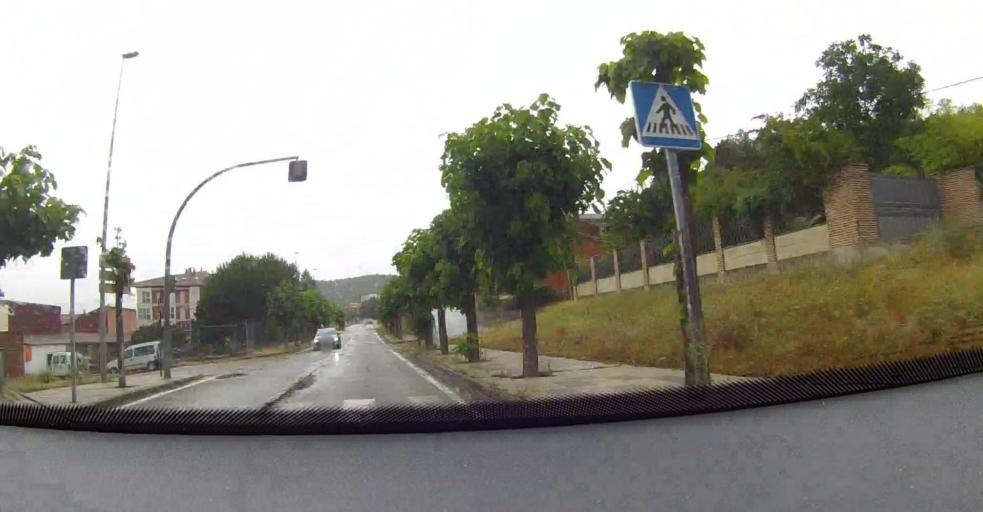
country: ES
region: Castille and Leon
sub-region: Provincia de Palencia
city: Saldana
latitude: 42.5229
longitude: -4.7334
